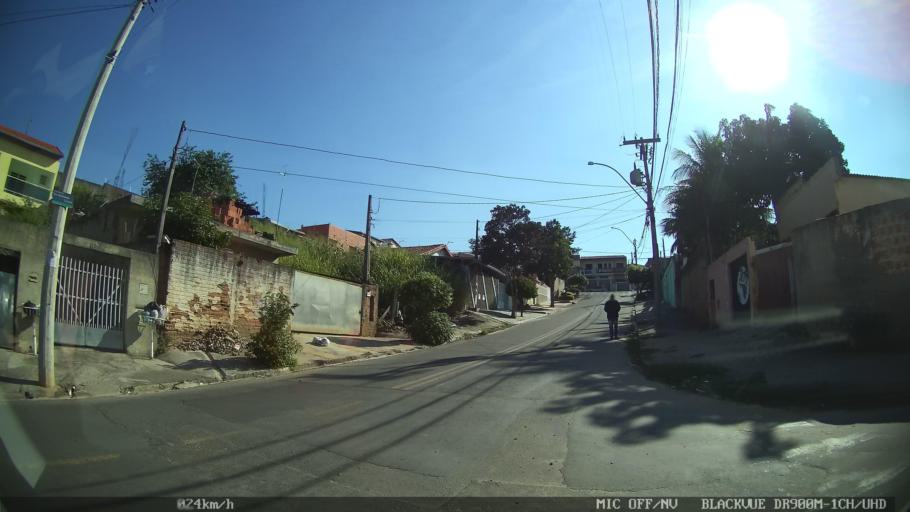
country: BR
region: Sao Paulo
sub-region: Campinas
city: Campinas
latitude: -22.9553
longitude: -47.0899
